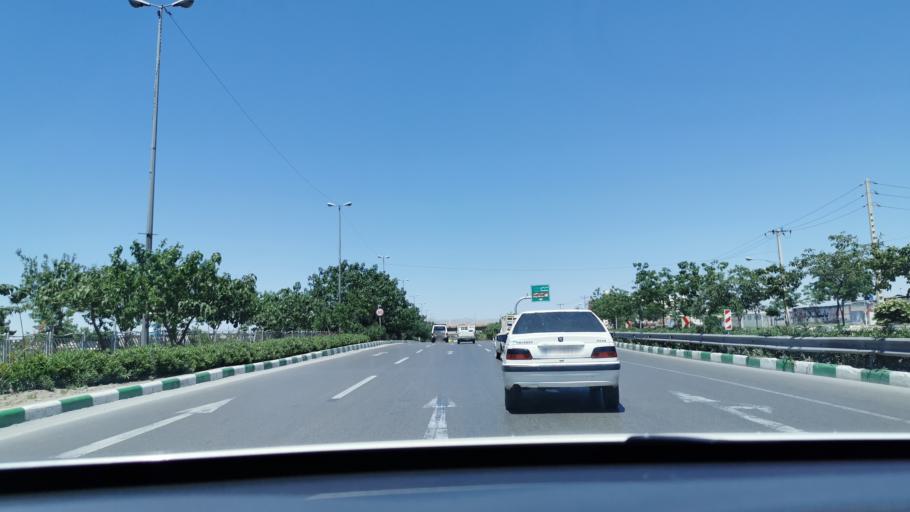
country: IR
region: Razavi Khorasan
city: Mashhad
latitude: 36.2645
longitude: 59.6527
